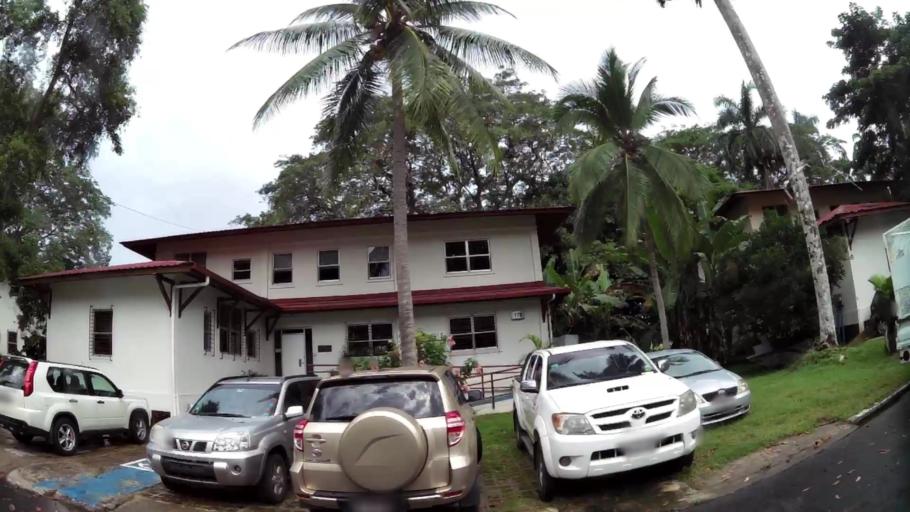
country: PA
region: Panama
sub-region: Distrito de Panama
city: Ancon
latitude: 8.9985
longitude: -79.5803
